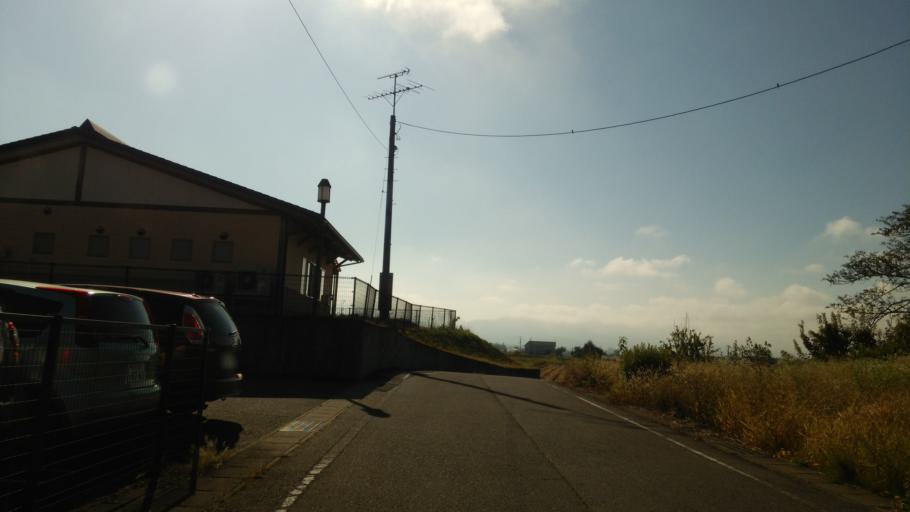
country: JP
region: Fukushima
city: Kitakata
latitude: 37.5495
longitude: 139.9251
